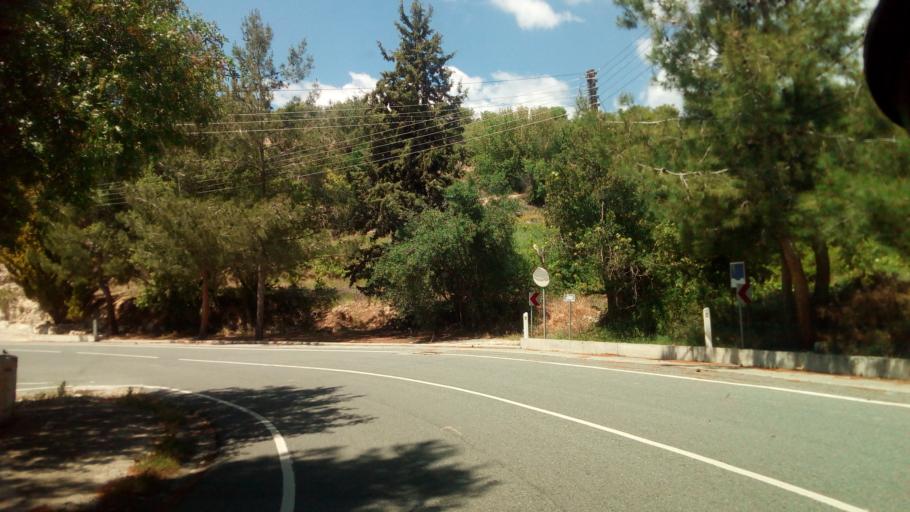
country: CY
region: Limassol
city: Pachna
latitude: 34.8441
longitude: 32.7720
